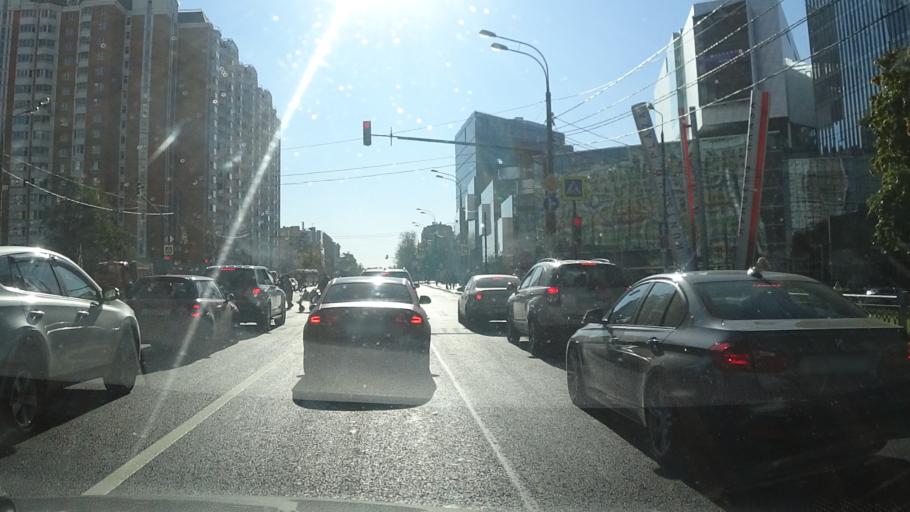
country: RU
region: Moskovskaya
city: Bol'shaya Setun'
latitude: 55.7394
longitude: 37.4133
